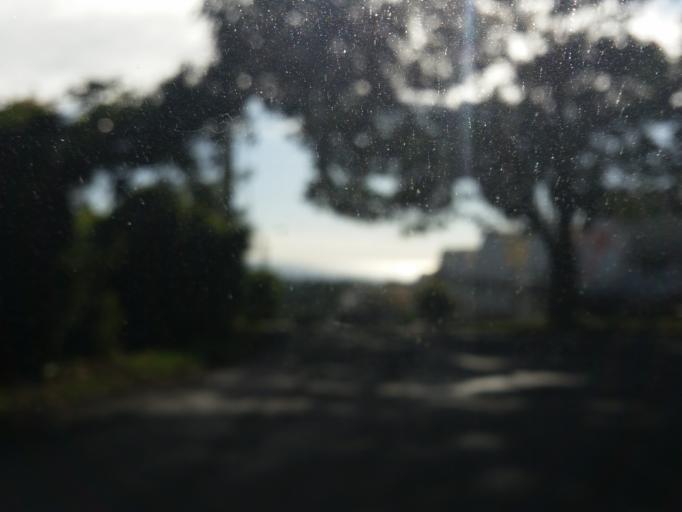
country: RE
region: Reunion
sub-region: Reunion
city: Sainte-Marie
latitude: -20.9115
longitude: 55.5028
